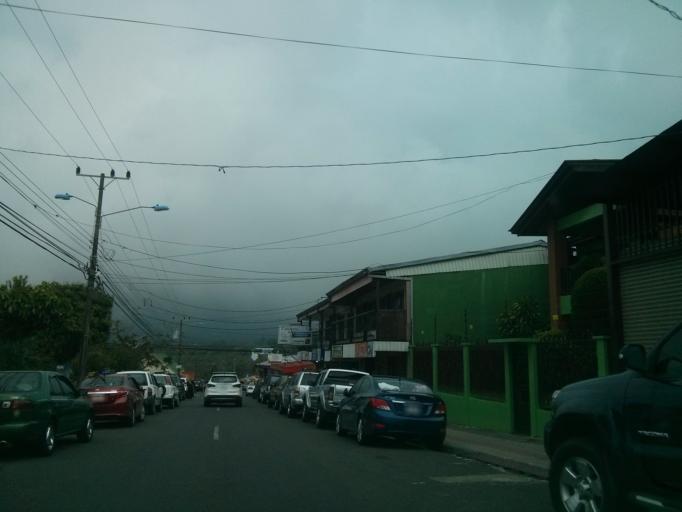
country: CR
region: Heredia
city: Angeles
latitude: 10.0178
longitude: -84.0557
